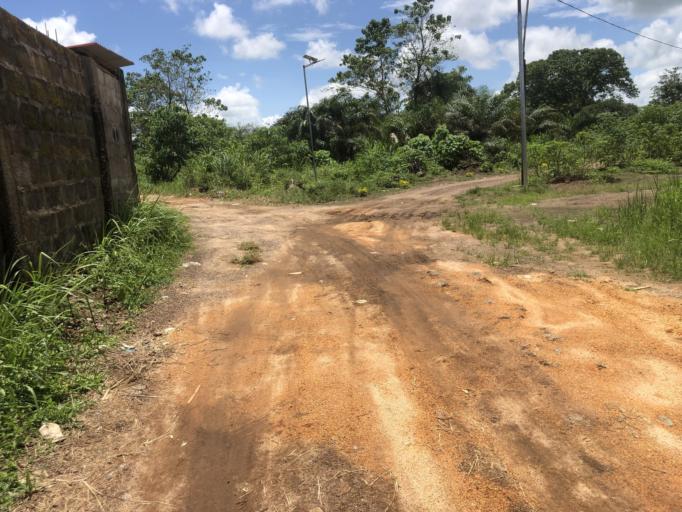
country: SL
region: Northern Province
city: Makeni
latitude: 8.8570
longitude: -12.0469
